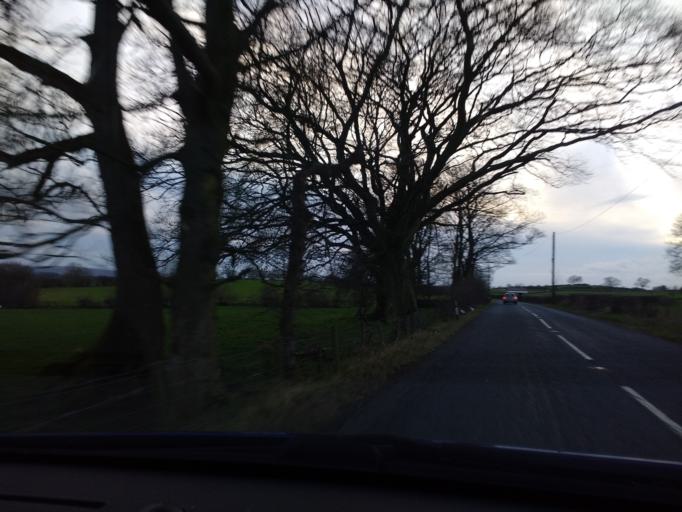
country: GB
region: England
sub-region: North Yorkshire
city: Ingleton
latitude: 54.1534
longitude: -2.4975
